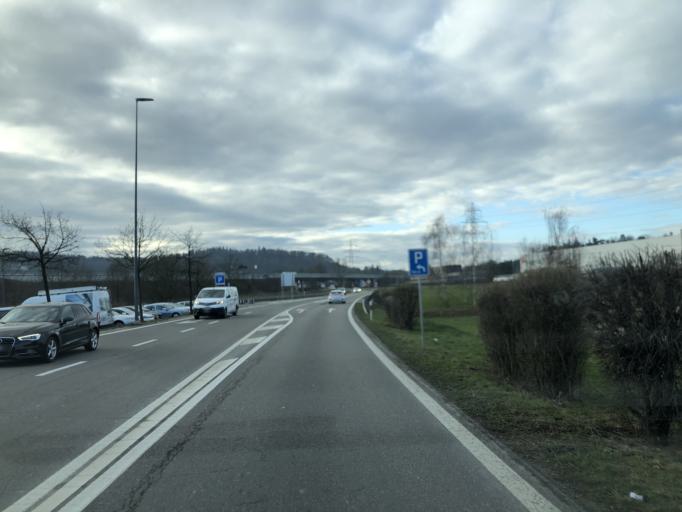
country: CH
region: Aargau
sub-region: Bezirk Lenzburg
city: Othmarsingen
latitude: 47.4208
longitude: 8.2230
